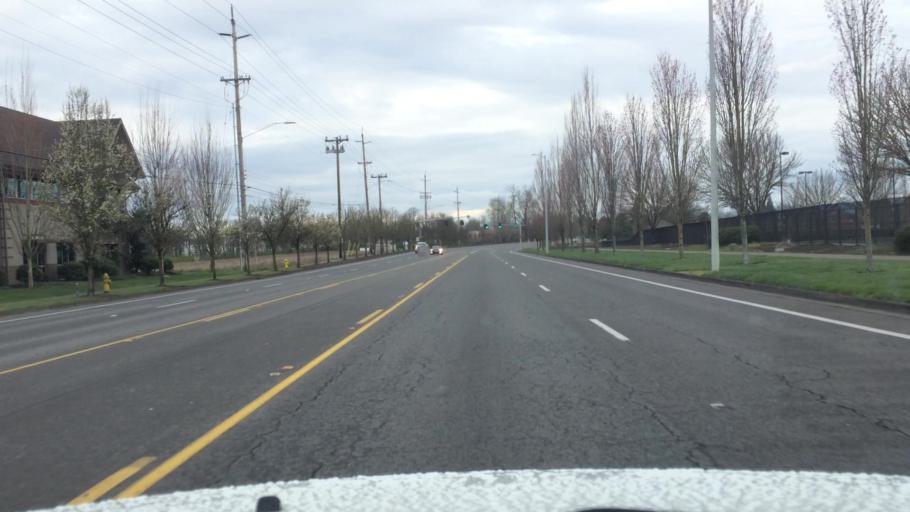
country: US
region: Oregon
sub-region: Marion County
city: Four Corners
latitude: 44.9280
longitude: -122.9960
